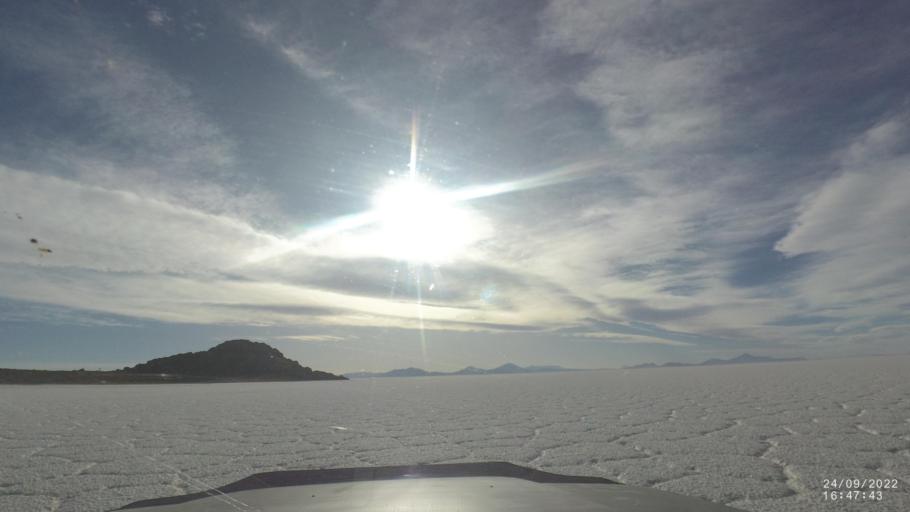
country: BO
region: Potosi
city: Colchani
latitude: -20.1320
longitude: -67.8063
